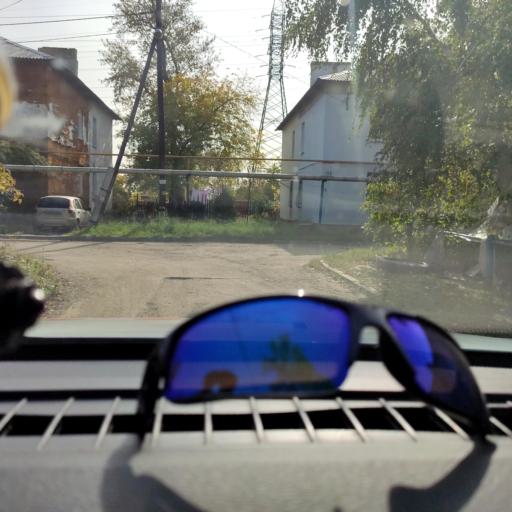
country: RU
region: Samara
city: Samara
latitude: 53.1327
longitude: 50.1209
